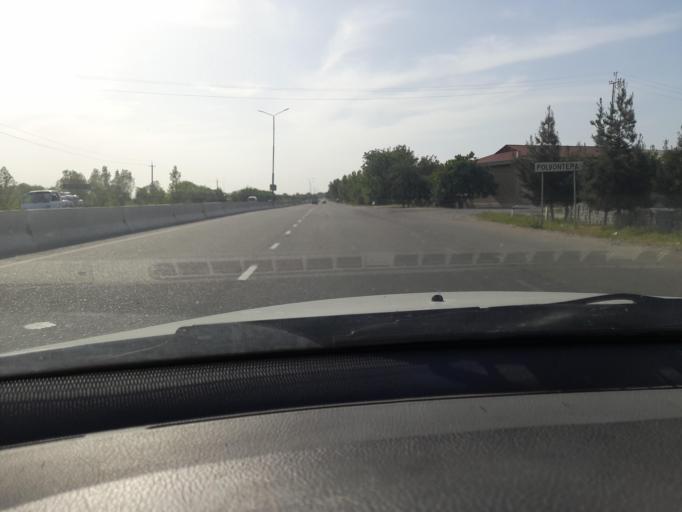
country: UZ
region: Samarqand
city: Kattaqo'rg'on
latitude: 39.9241
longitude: 66.2271
